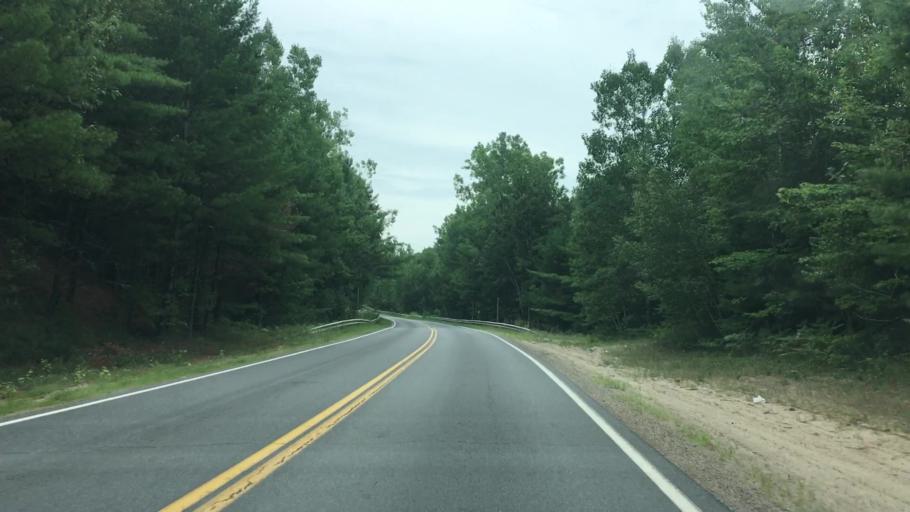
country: US
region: New York
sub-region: Essex County
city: Keeseville
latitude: 44.4746
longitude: -73.5949
